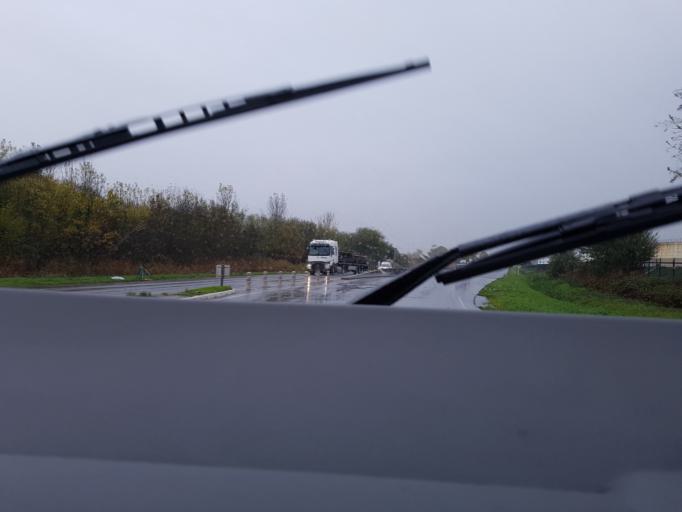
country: FR
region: Aquitaine
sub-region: Departement de la Gironde
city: Saint-Louis-de-Montferrand
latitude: 44.9198
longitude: -0.5431
